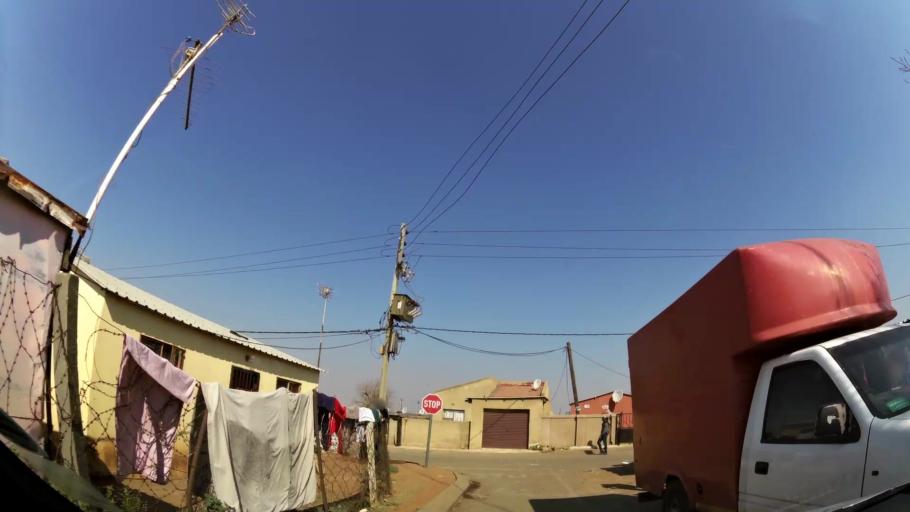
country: ZA
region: Gauteng
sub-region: Ekurhuleni Metropolitan Municipality
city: Boksburg
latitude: -26.2305
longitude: 28.2995
